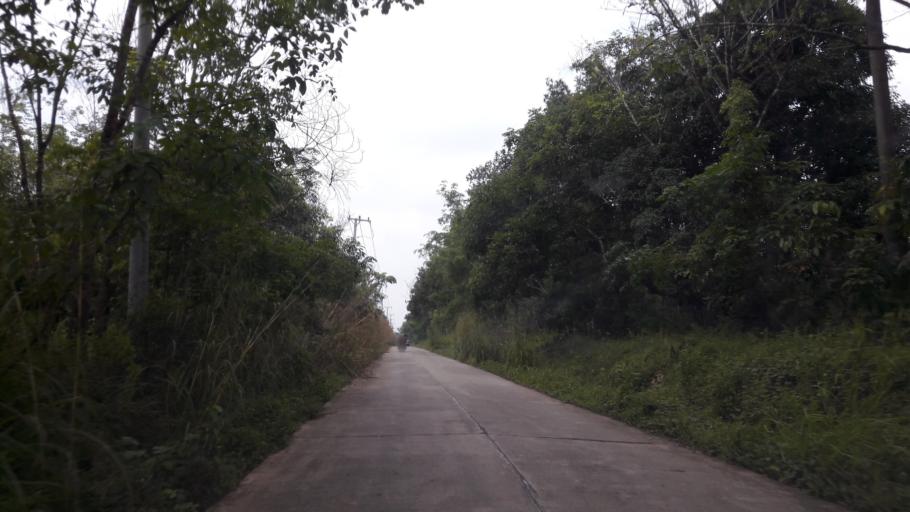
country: ID
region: South Sumatra
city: Gunungmenang
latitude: -3.2333
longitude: 104.1195
